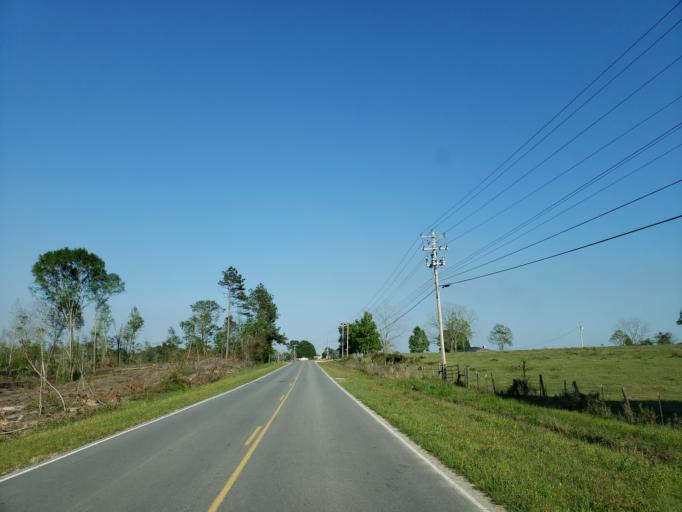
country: US
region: Mississippi
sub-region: Perry County
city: Richton
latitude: 31.4818
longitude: -89.0255
